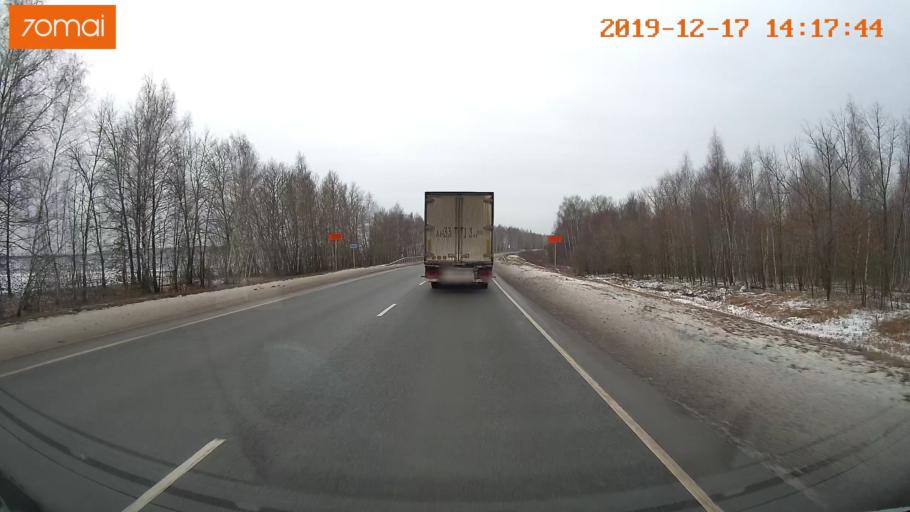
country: RU
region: Rjazan
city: Zakharovo
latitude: 54.4635
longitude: 39.4531
